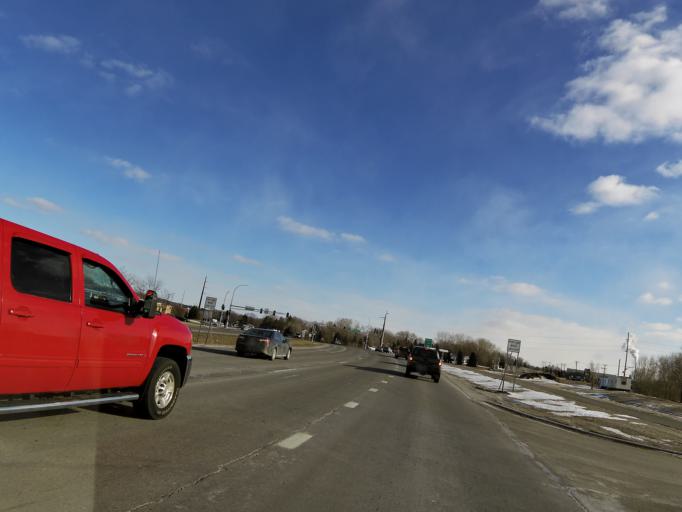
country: US
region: Minnesota
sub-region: Dakota County
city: Mendota Heights
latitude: 44.8468
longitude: -93.1256
